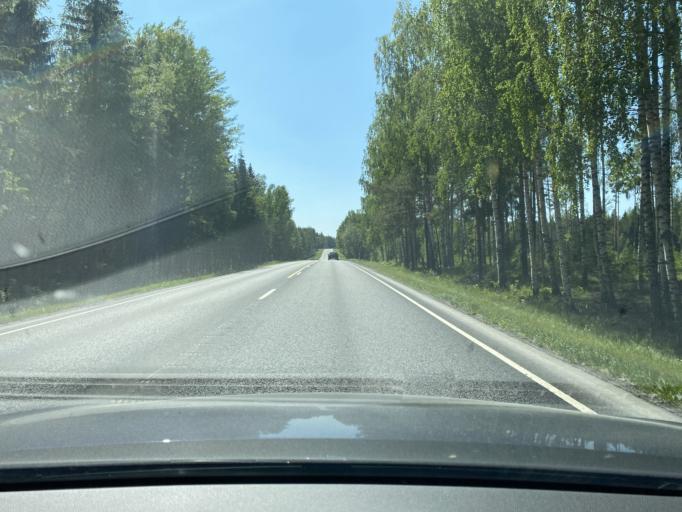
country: FI
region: Pirkanmaa
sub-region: Tampere
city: Nokia
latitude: 61.4125
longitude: 23.3079
